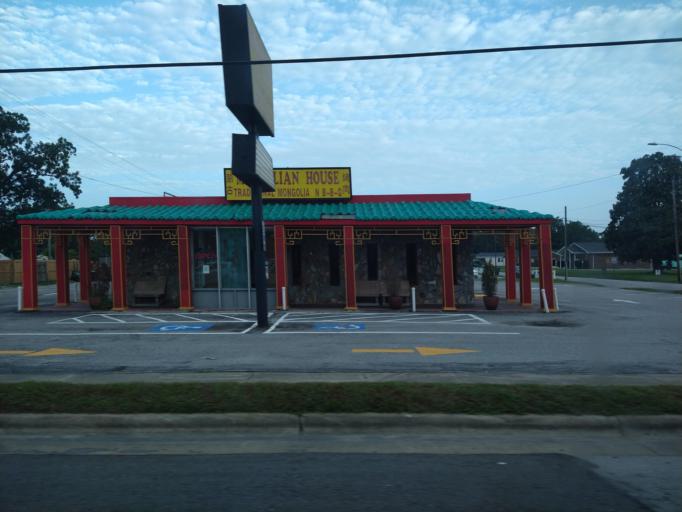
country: US
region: North Carolina
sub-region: Onslow County
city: Jacksonville
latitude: 34.7586
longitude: -77.4187
